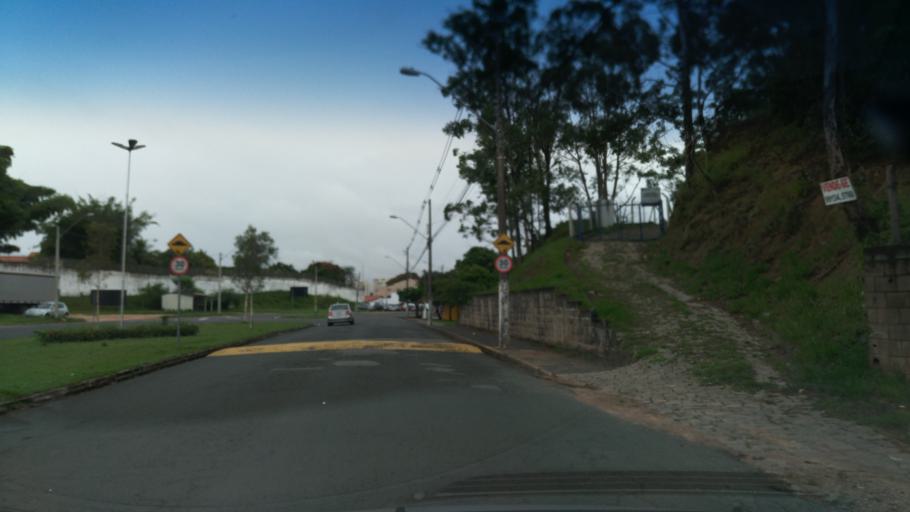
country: BR
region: Sao Paulo
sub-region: Valinhos
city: Valinhos
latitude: -22.9561
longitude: -47.0103
